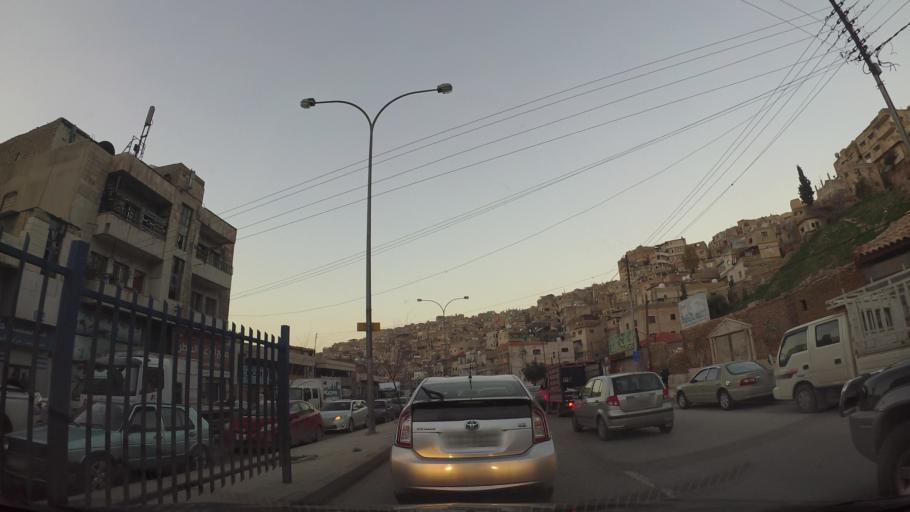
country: JO
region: Amman
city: Amman
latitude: 31.9370
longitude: 35.9236
